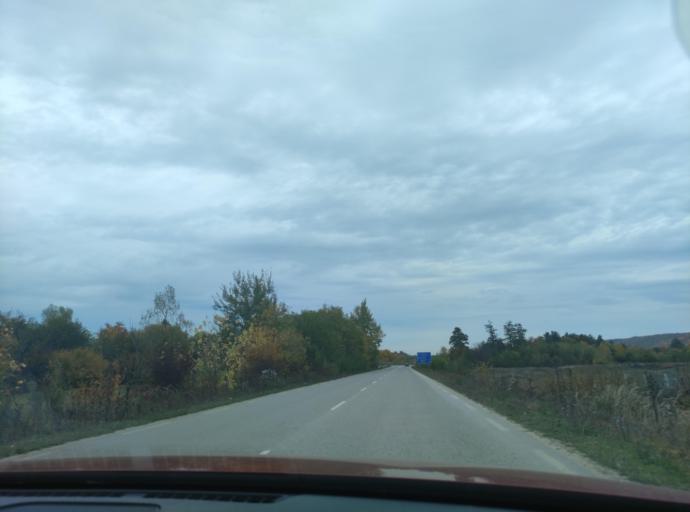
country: BG
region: Montana
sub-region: Obshtina Berkovitsa
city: Berkovitsa
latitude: 43.2411
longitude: 23.1633
